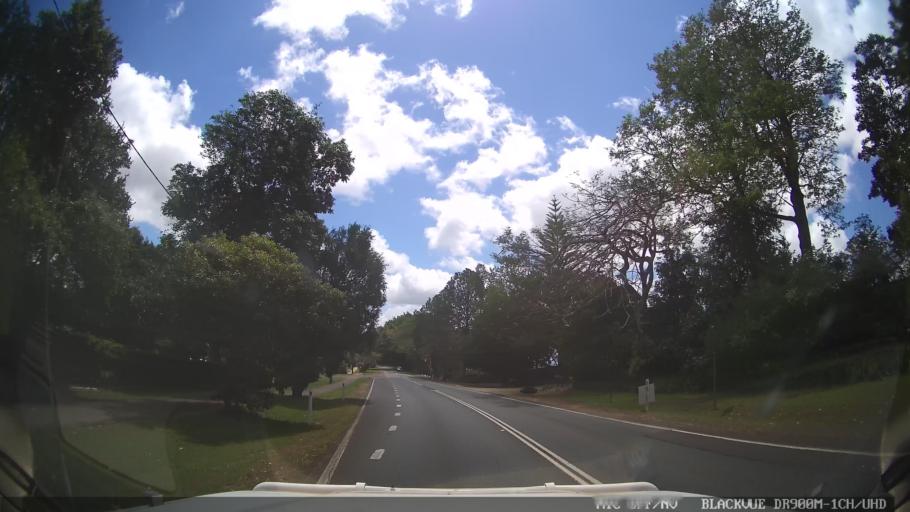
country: AU
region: Queensland
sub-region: Sunshine Coast
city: Nambour
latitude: -26.6625
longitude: 152.8830
